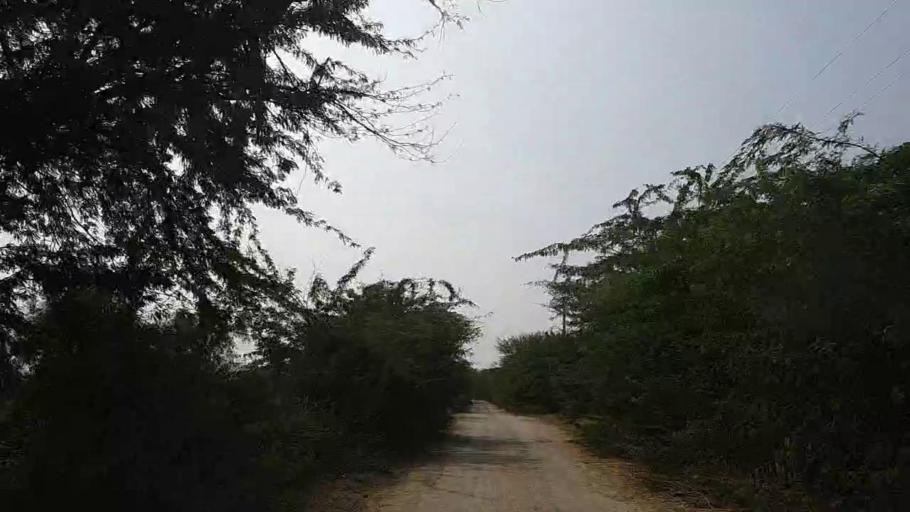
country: PK
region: Sindh
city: Mirpur Sakro
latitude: 24.6095
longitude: 67.7275
